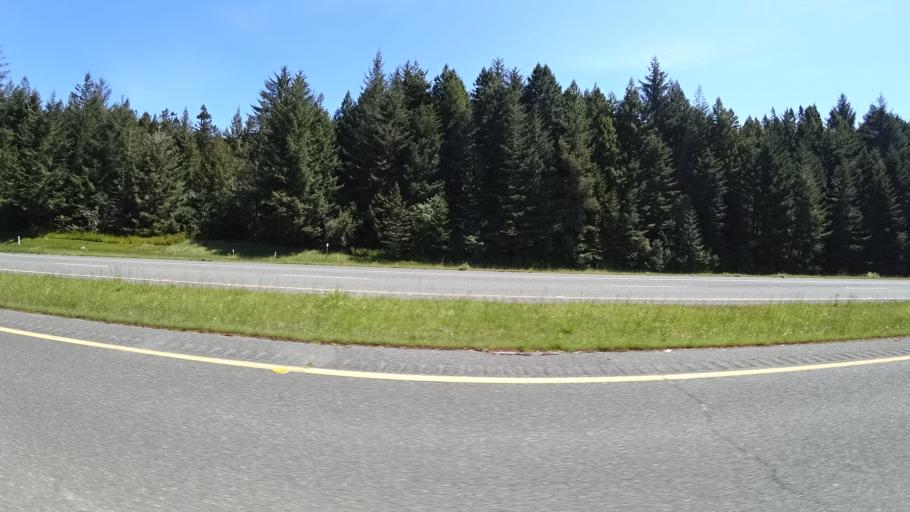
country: US
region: California
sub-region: Humboldt County
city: Westhaven-Moonstone
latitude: 41.0994
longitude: -124.1539
